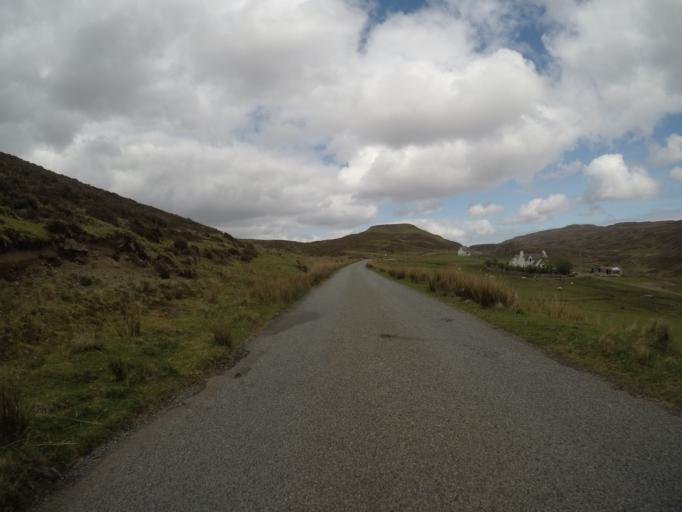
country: GB
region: Scotland
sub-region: Highland
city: Isle of Skye
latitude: 57.3733
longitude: -6.3770
